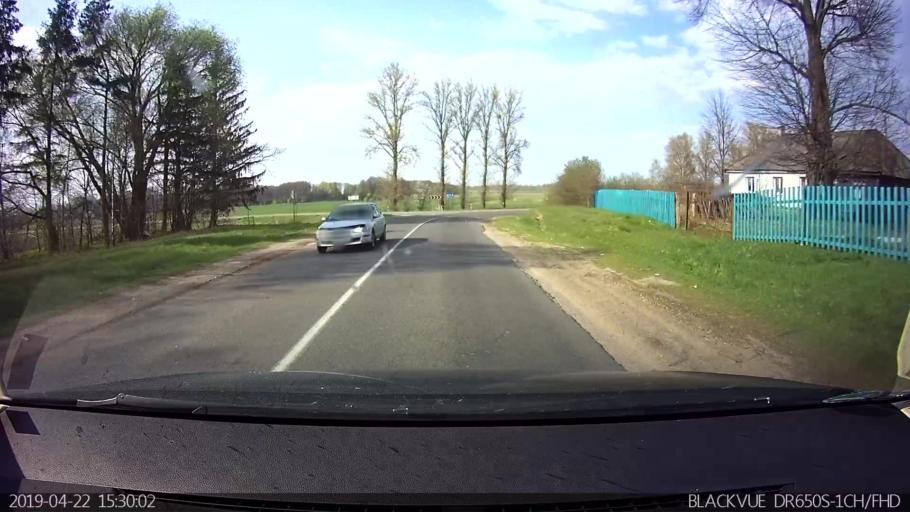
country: BY
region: Brest
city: Vysokaye
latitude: 52.3947
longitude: 23.3756
